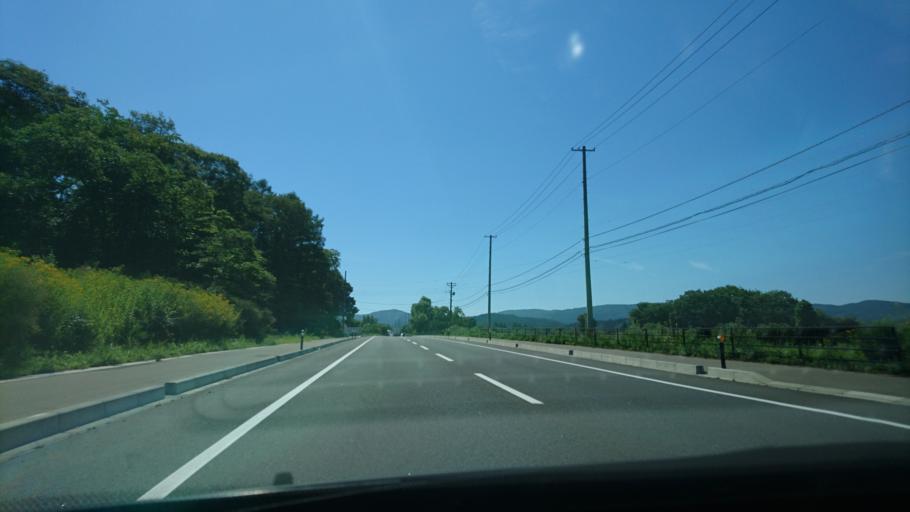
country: JP
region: Iwate
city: Tono
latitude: 39.3047
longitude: 141.5750
